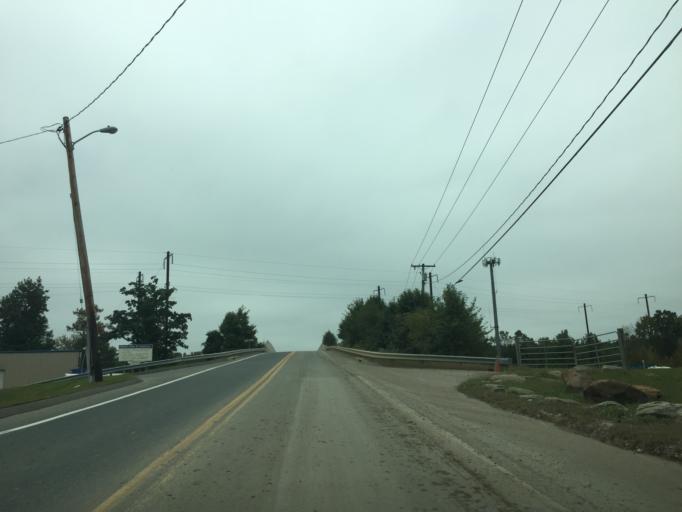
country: US
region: Maryland
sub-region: Baltimore County
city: Bowleys Quarters
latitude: 39.3474
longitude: -76.3942
